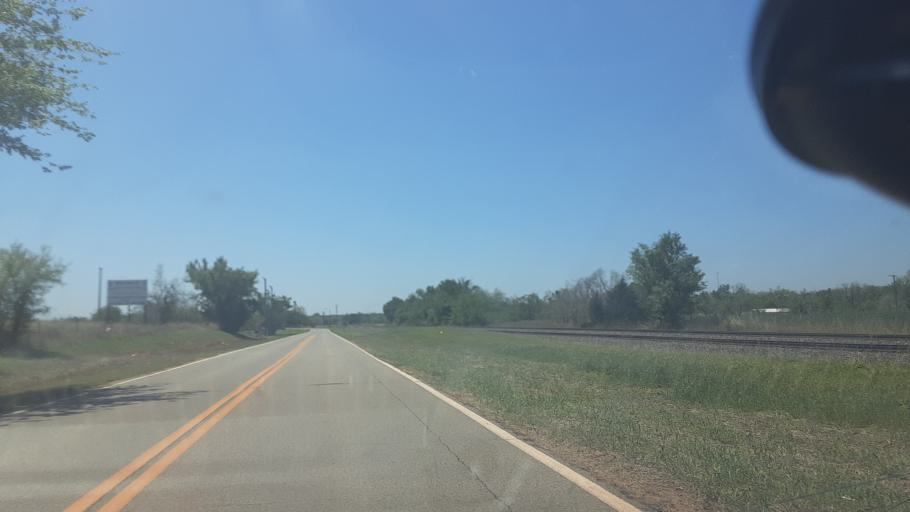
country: US
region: Oklahoma
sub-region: Logan County
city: Guthrie
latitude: 36.0712
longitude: -97.4058
